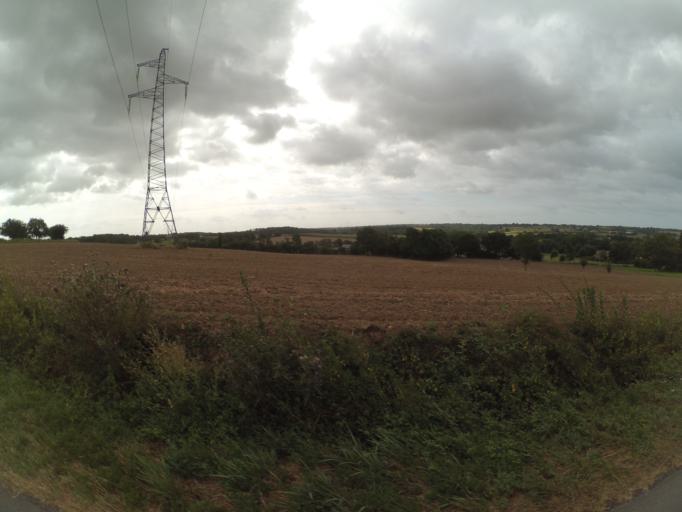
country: FR
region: Pays de la Loire
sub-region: Departement de Maine-et-Loire
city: Montfaucon-Montigne
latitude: 47.1056
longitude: -1.1160
